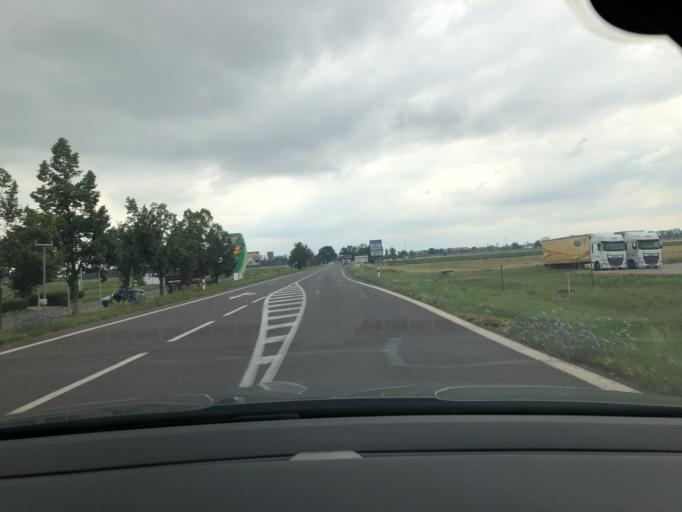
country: CZ
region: South Moravian
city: Hevlin
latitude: 48.7354
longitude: 16.3826
